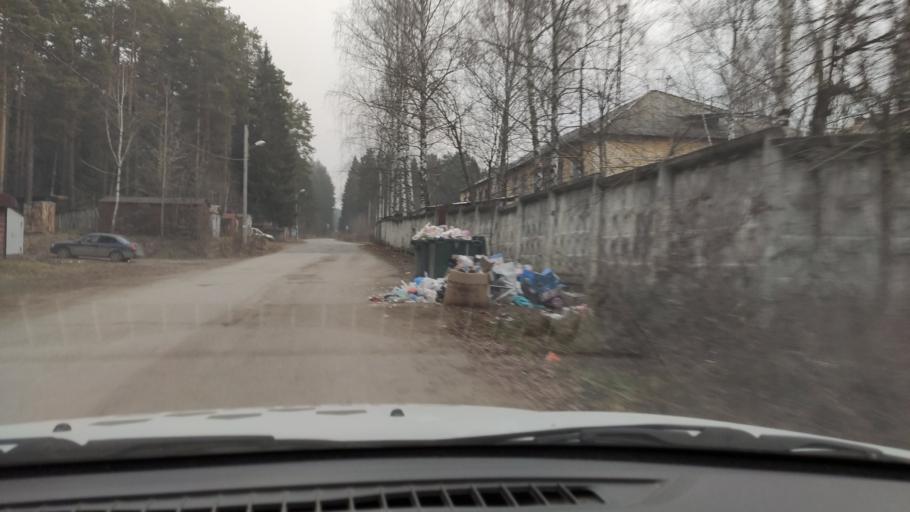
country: RU
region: Perm
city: Kondratovo
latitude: 58.0453
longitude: 56.1382
